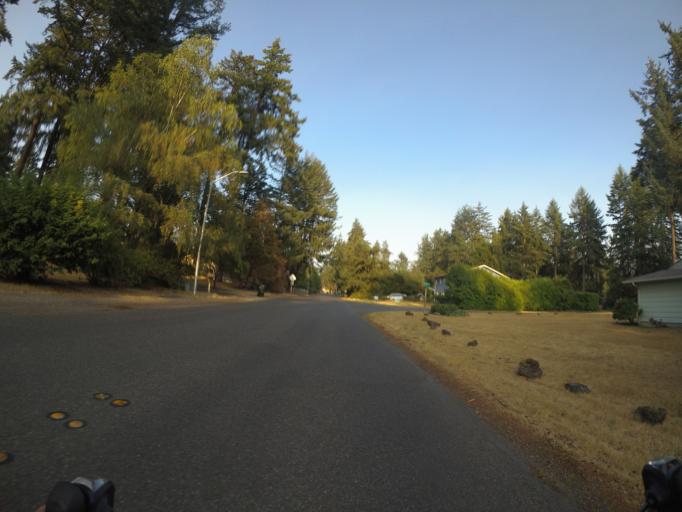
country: US
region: Washington
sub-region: Pierce County
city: Lakewood
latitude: 47.1489
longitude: -122.5197
